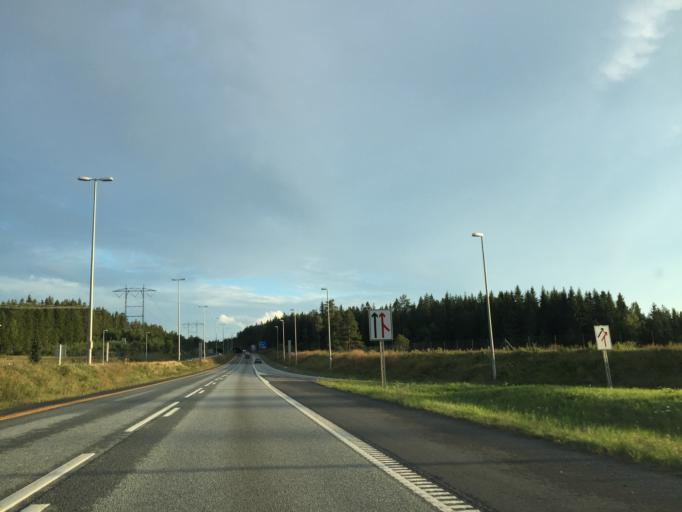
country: NO
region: Akershus
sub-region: Oppegard
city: Kolbotn
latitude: 59.7952
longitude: 10.8421
